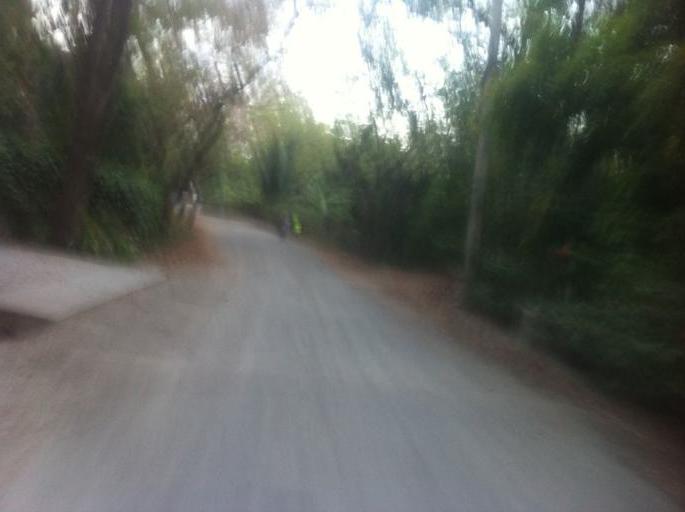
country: CR
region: Guanacaste
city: Samara
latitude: 9.9495
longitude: -85.6679
